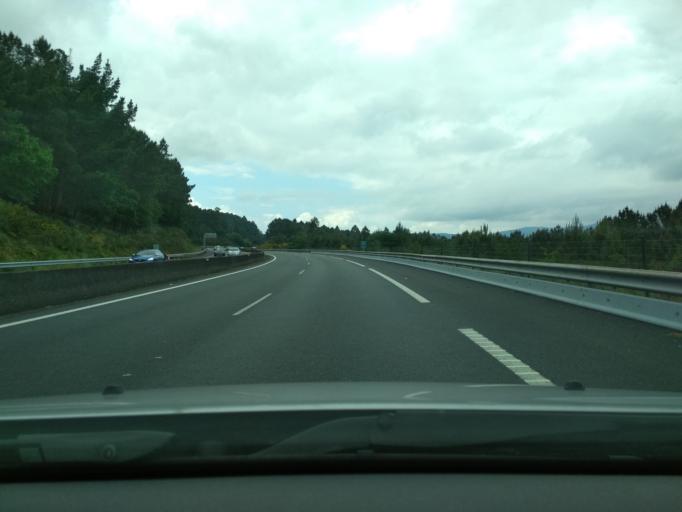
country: ES
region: Galicia
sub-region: Provincia da Coruna
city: Padron
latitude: 42.7949
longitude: -8.6373
